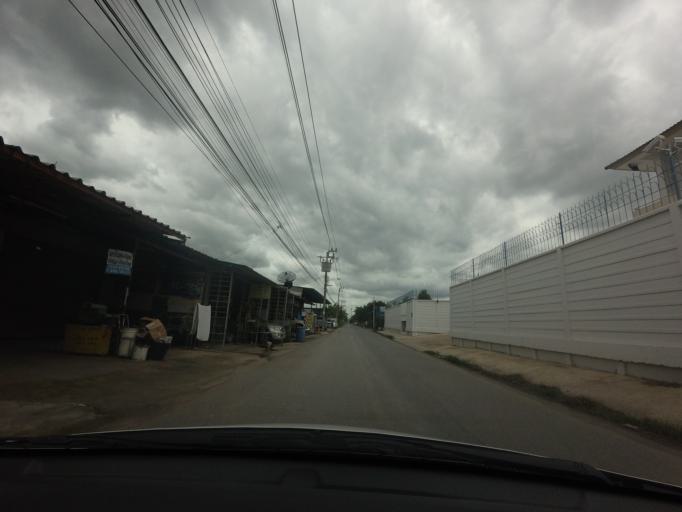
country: TH
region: Bangkok
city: Lat Krabang
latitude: 13.7755
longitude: 100.7731
